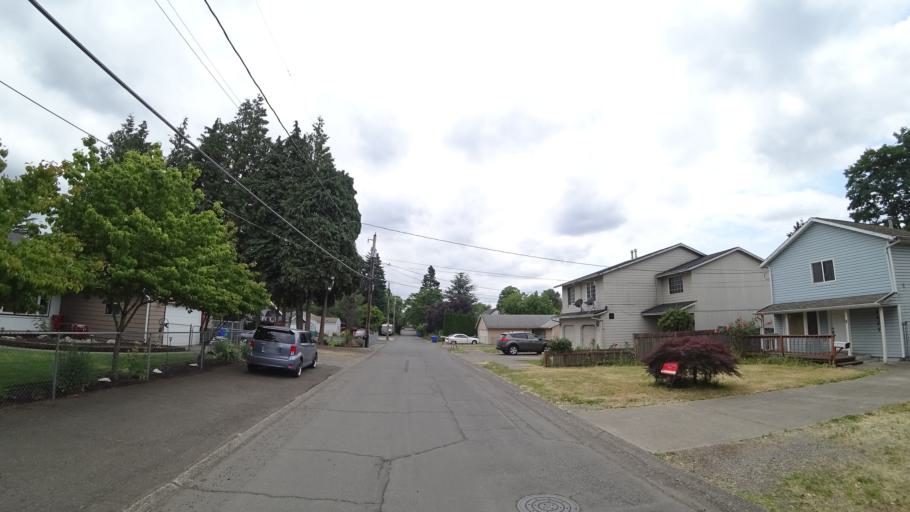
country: US
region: Oregon
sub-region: Multnomah County
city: Lents
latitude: 45.5073
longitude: -122.5705
